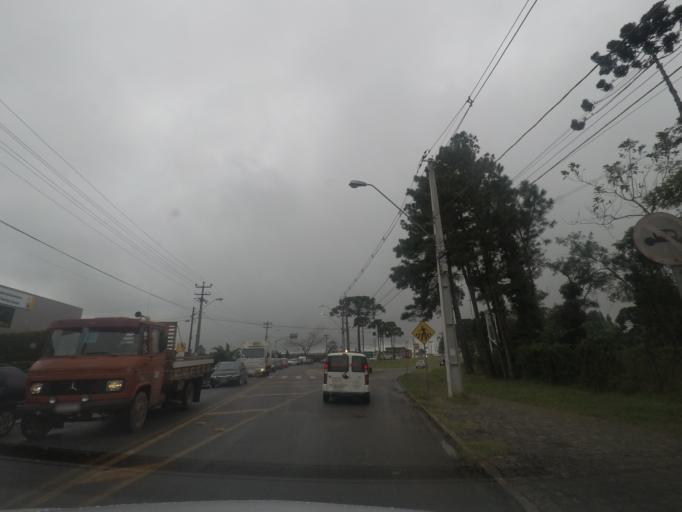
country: BR
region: Parana
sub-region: Quatro Barras
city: Quatro Barras
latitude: -25.3513
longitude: -49.0830
